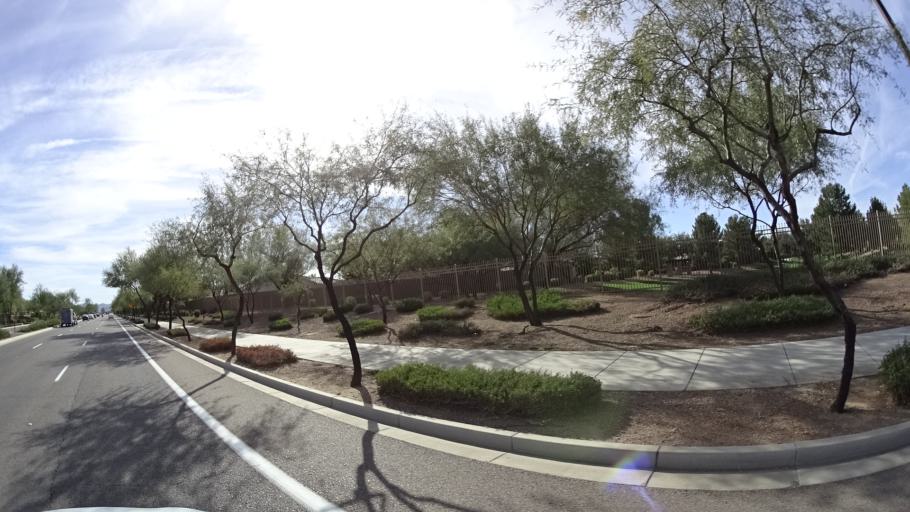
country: US
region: Arizona
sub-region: Maricopa County
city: Queen Creek
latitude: 33.2563
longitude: -111.6860
